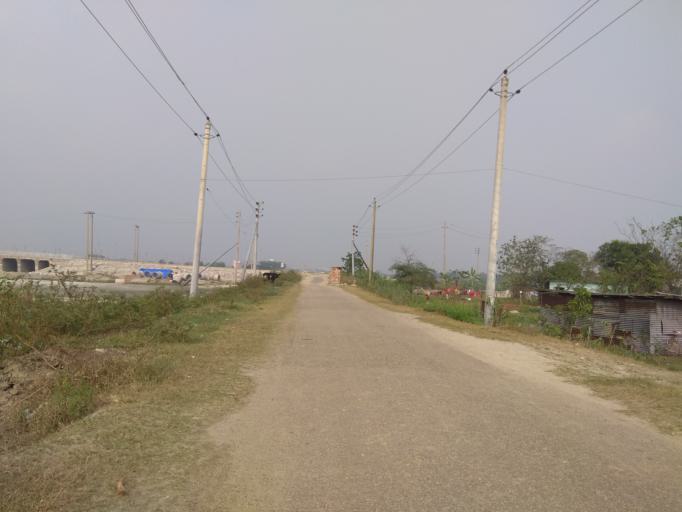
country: BD
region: Dhaka
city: Tungi
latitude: 23.8587
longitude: 90.3727
